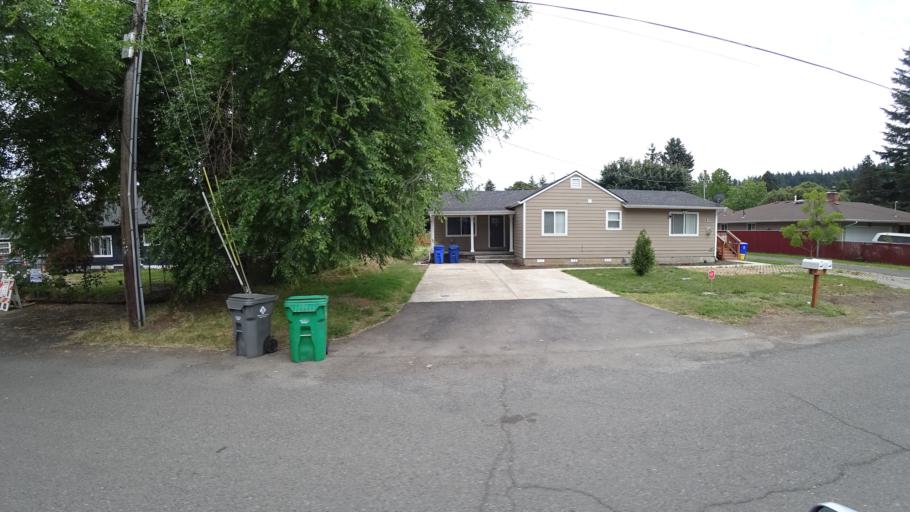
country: US
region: Oregon
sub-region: Clackamas County
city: Happy Valley
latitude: 45.4965
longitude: -122.5184
